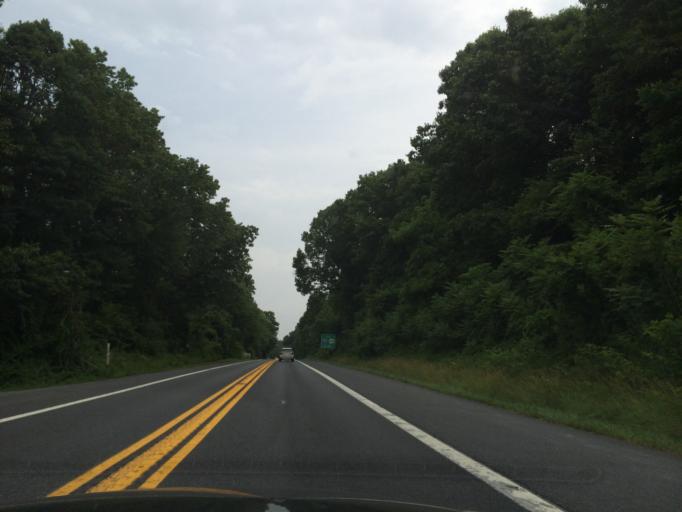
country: US
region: Maryland
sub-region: Carroll County
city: Sykesville
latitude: 39.2940
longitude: -76.9535
